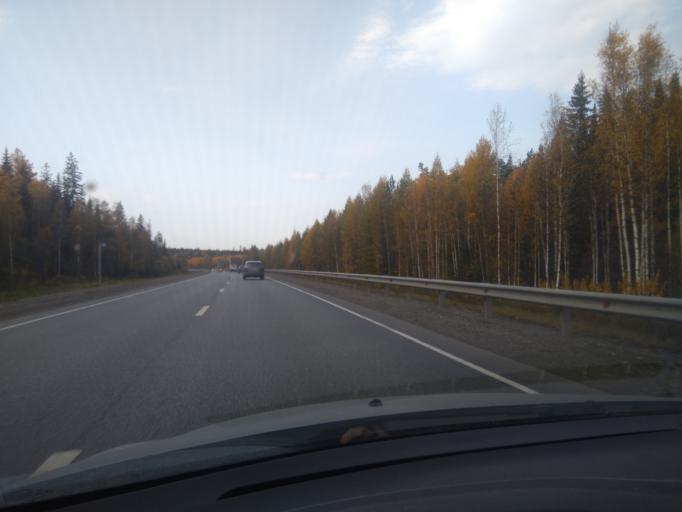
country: RU
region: Sverdlovsk
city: Druzhinino
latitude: 56.8259
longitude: 59.5854
